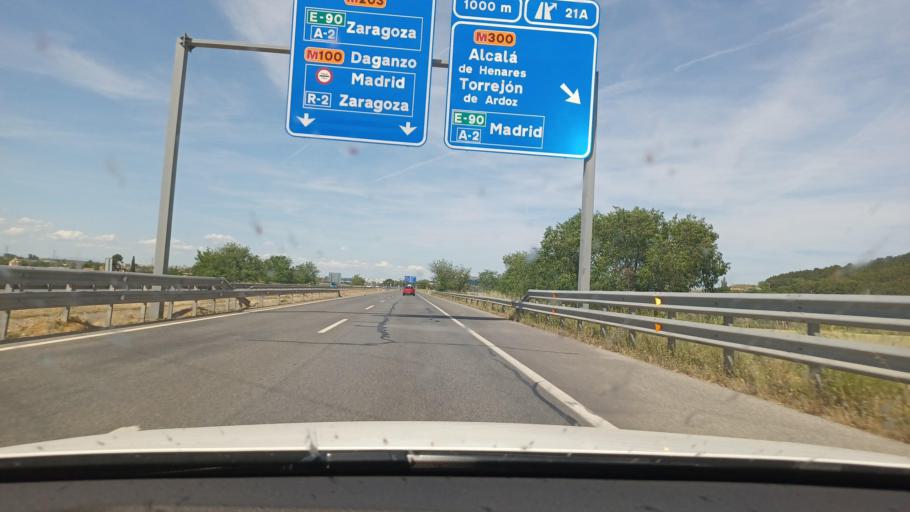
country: ES
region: Madrid
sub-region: Provincia de Madrid
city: Torrejon de Ardoz
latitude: 40.4556
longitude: -3.4168
